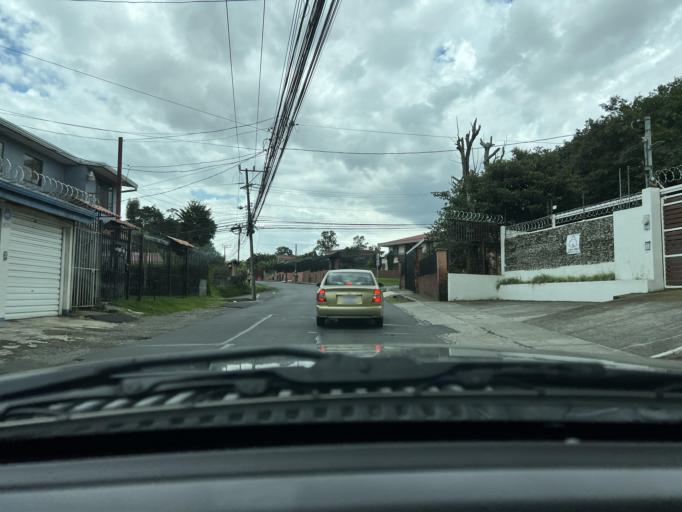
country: CR
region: San Jose
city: Granadilla
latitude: 9.9398
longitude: -84.0249
